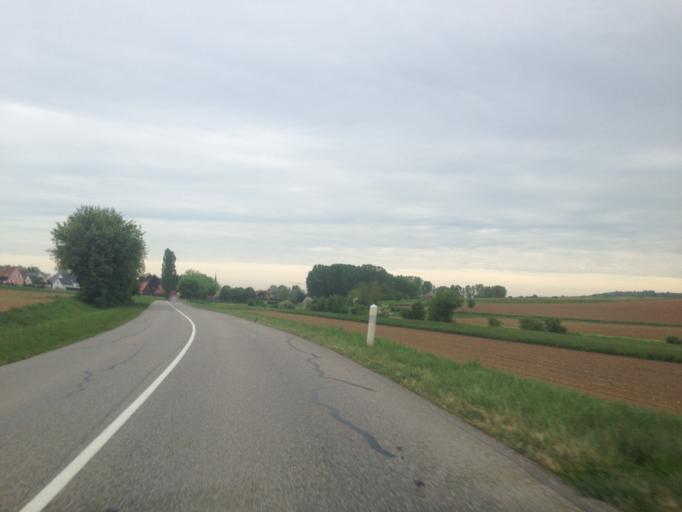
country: FR
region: Alsace
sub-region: Departement du Bas-Rhin
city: Hochfelden
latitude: 48.7773
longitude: 7.5688
